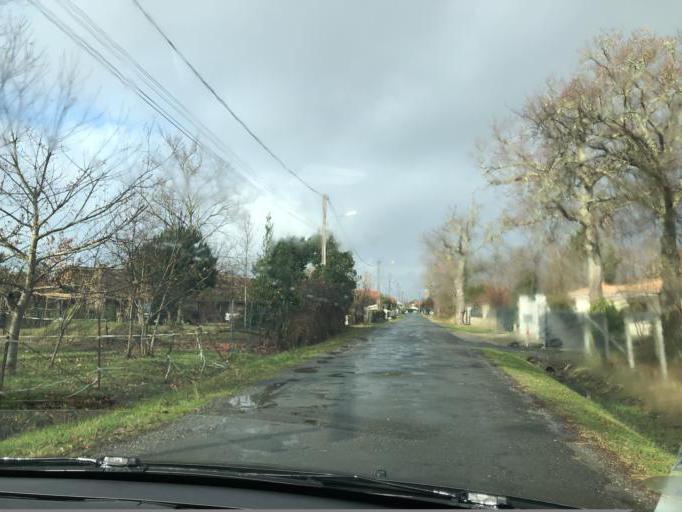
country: FR
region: Aquitaine
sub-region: Departement de la Gironde
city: Hourtin
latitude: 45.1813
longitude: -1.0544
